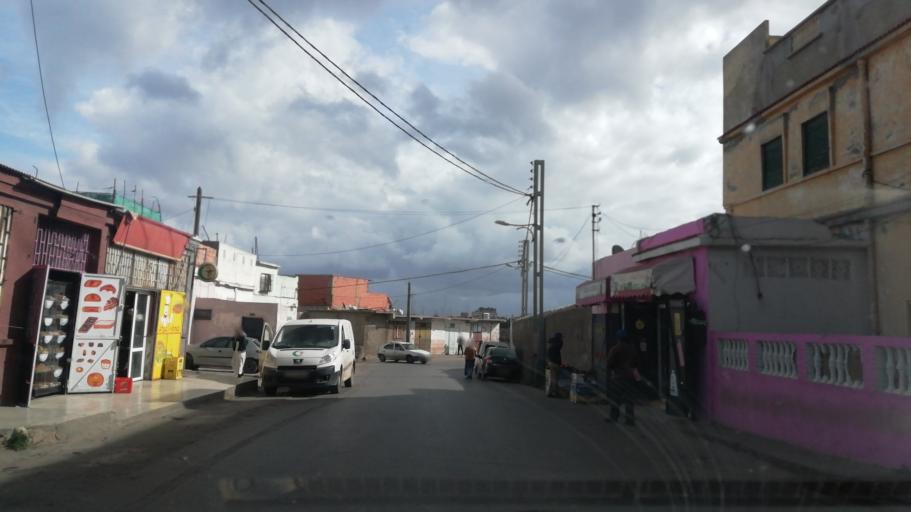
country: DZ
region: Oran
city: Oran
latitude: 35.7000
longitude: -0.6596
